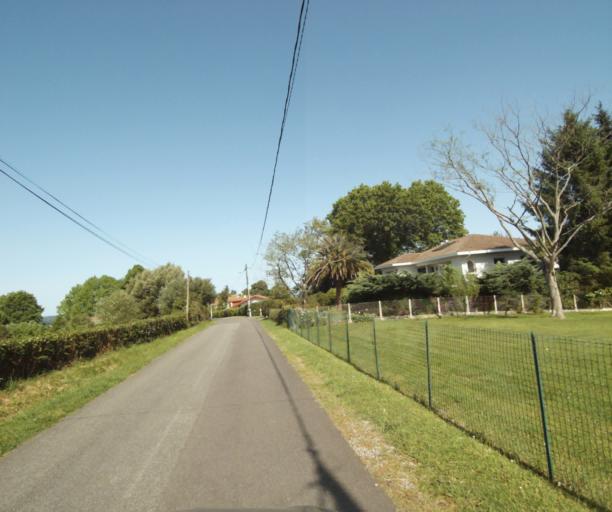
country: FR
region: Aquitaine
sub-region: Departement des Pyrenees-Atlantiques
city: Villefranque
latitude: 43.4562
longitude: -1.4424
